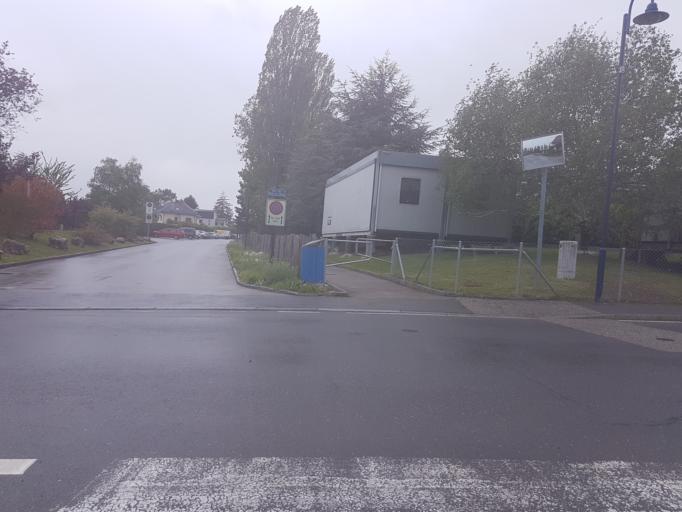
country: CH
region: Vaud
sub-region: Morges District
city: Preverenges
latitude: 46.5152
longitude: 6.5277
